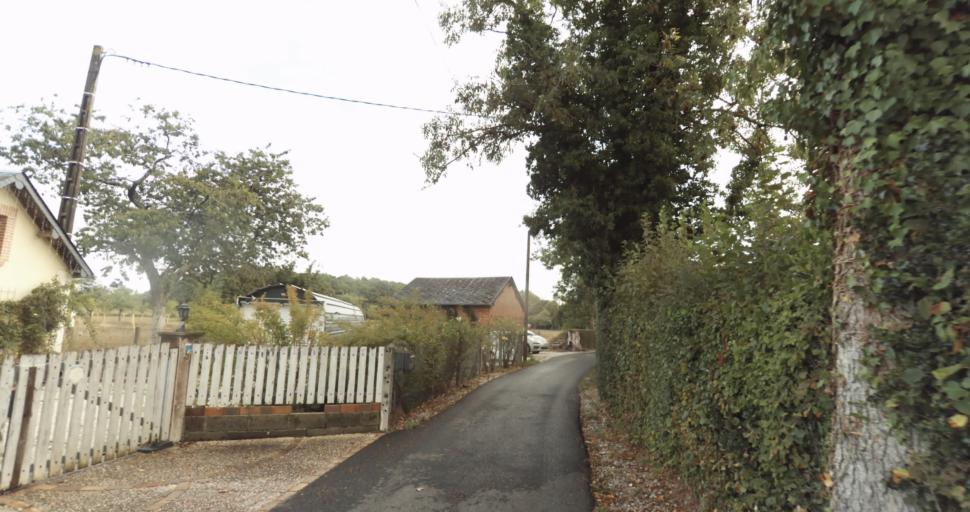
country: FR
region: Lower Normandy
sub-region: Departement de l'Orne
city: Vimoutiers
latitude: 48.9041
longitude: 0.2457
